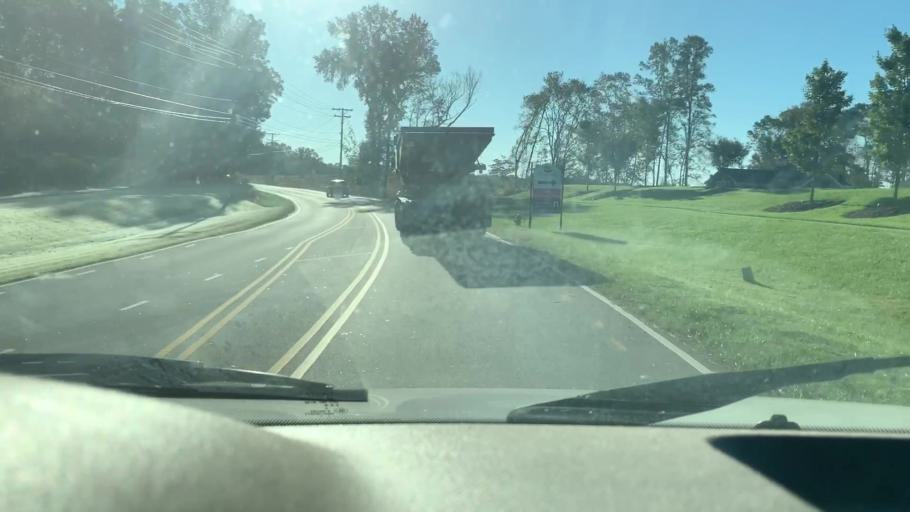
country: US
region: North Carolina
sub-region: Mecklenburg County
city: Huntersville
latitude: 35.4205
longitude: -80.7528
